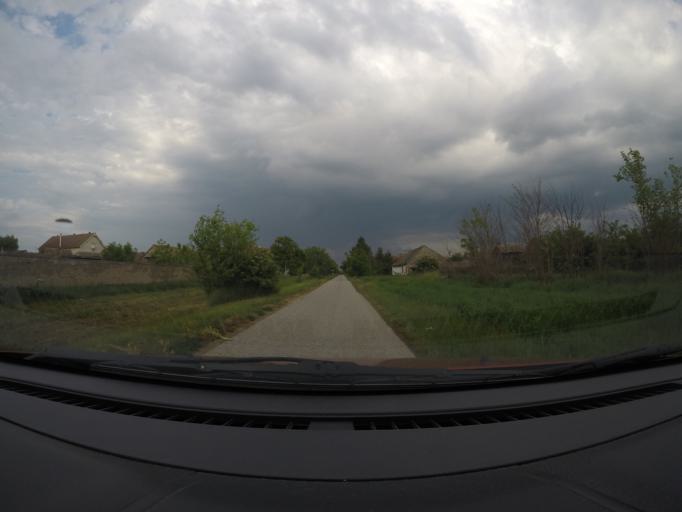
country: RS
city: Uzdin
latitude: 45.2028
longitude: 20.6146
